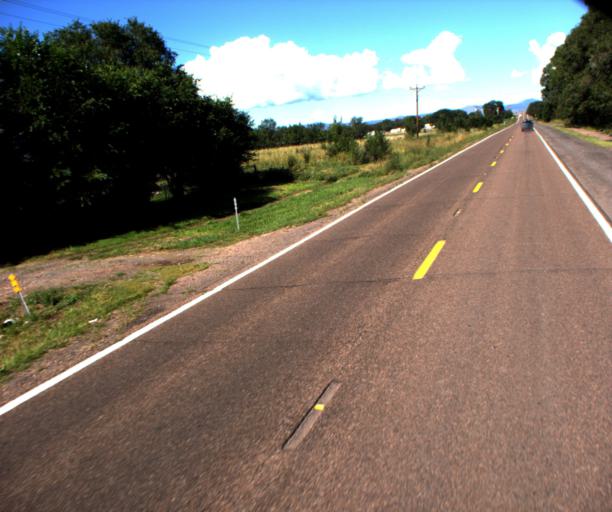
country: US
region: Arizona
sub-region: Apache County
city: Eagar
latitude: 34.1110
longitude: -109.2744
